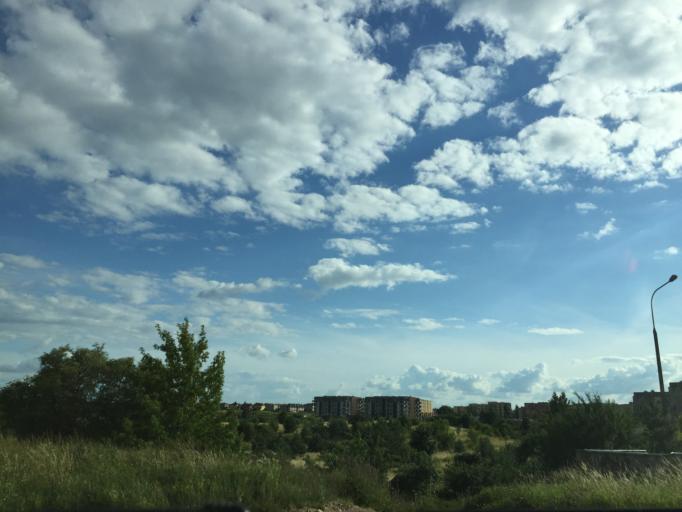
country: PL
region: Podlasie
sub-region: Suwalki
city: Suwalki
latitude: 54.1193
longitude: 22.9532
